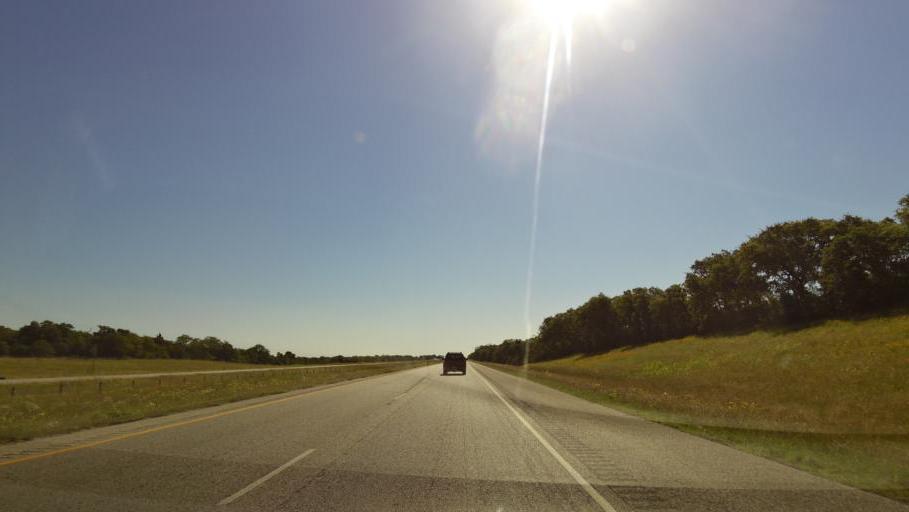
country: US
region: Texas
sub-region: Gonzales County
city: Gonzales
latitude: 29.6523
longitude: -97.4652
